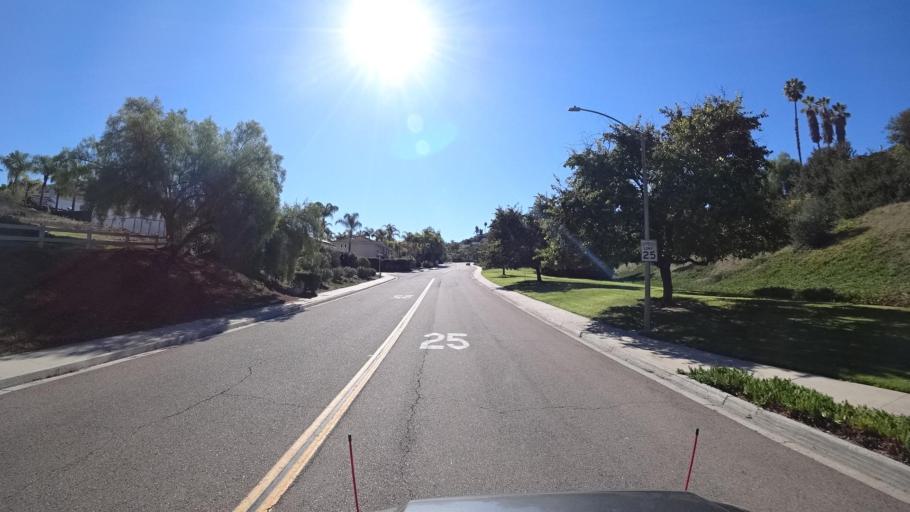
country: US
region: California
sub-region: San Diego County
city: Bonita
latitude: 32.6649
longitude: -117.0154
